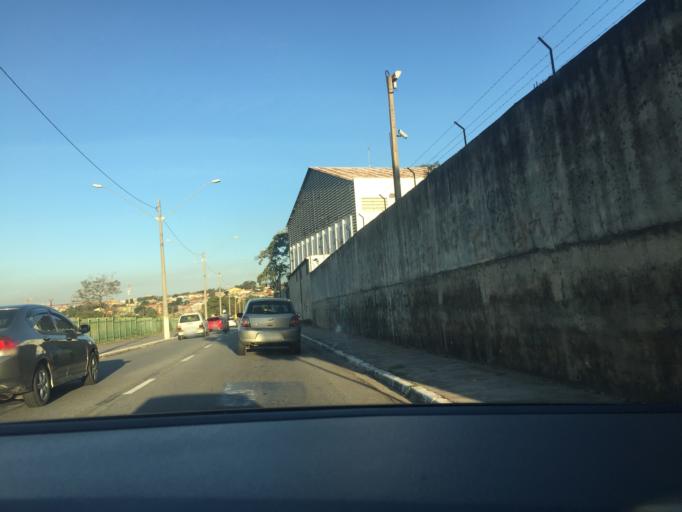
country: BR
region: Sao Paulo
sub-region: Jundiai
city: Jundiai
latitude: -23.2020
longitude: -46.8654
